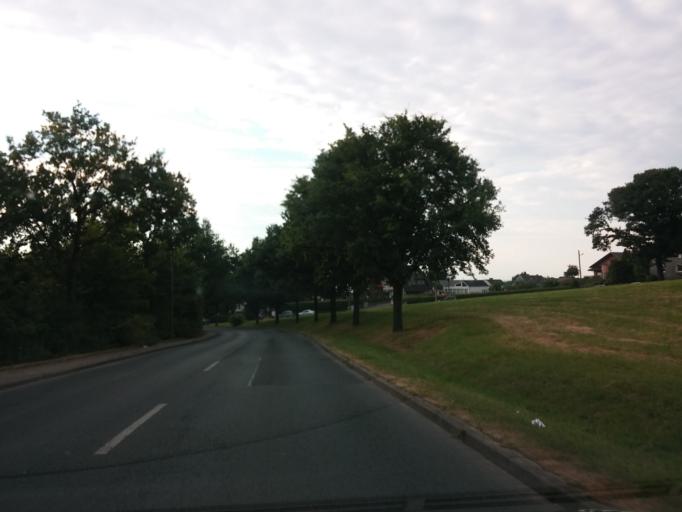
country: DE
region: North Rhine-Westphalia
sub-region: Regierungsbezirk Arnsberg
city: Bochum
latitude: 51.5065
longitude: 7.2230
